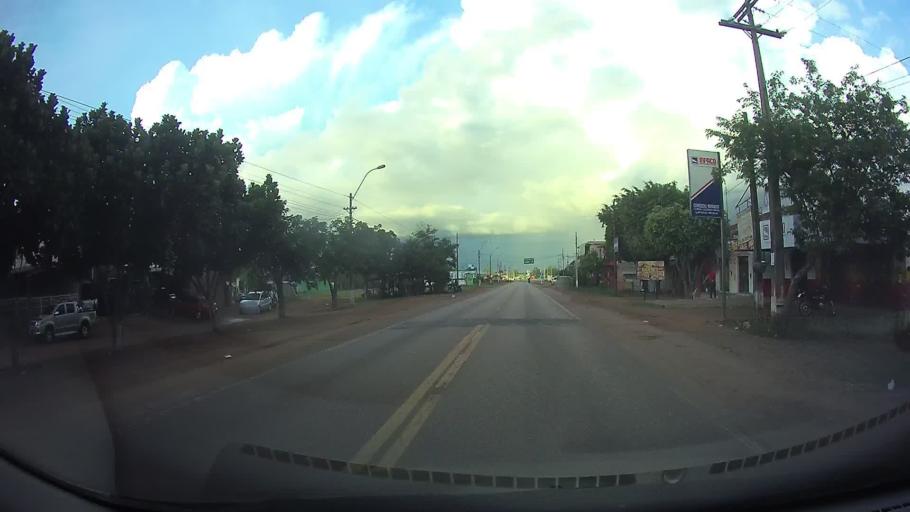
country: PY
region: Paraguari
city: Carapegua
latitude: -25.7662
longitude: -57.2366
